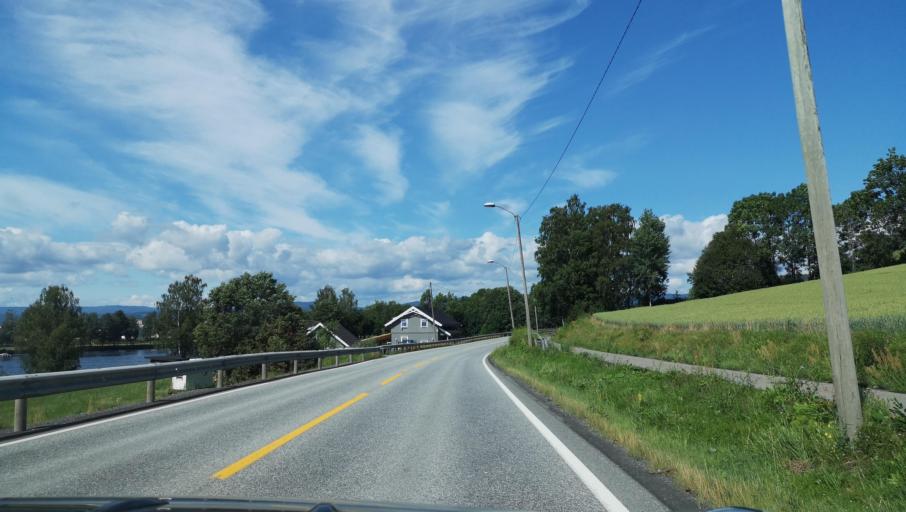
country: NO
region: Buskerud
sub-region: Nedre Eiker
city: Mjondalen
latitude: 59.7636
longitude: 9.9700
